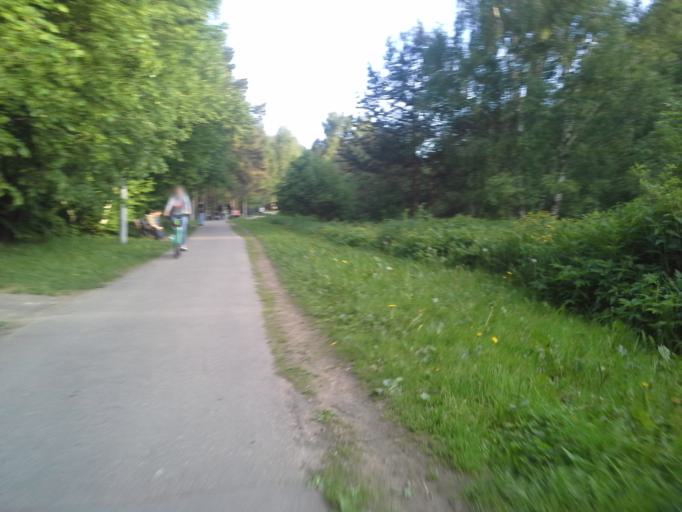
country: RU
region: Moscow
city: Nikulino
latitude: 55.6557
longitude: 37.4603
